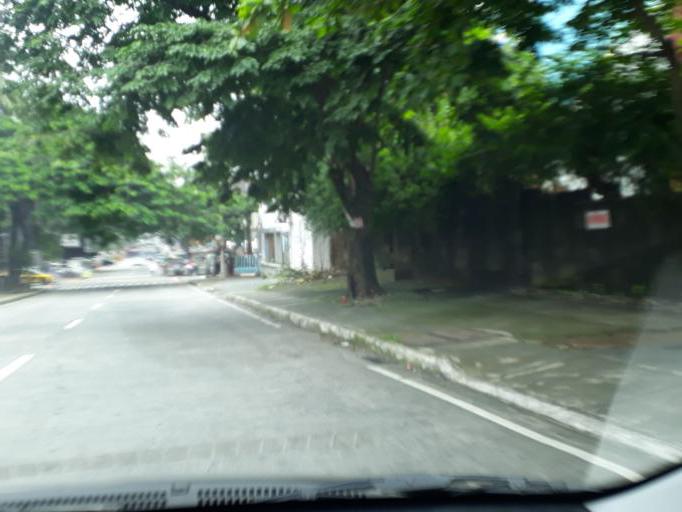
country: PH
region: Calabarzon
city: Del Monte
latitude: 14.6371
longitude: 121.0344
